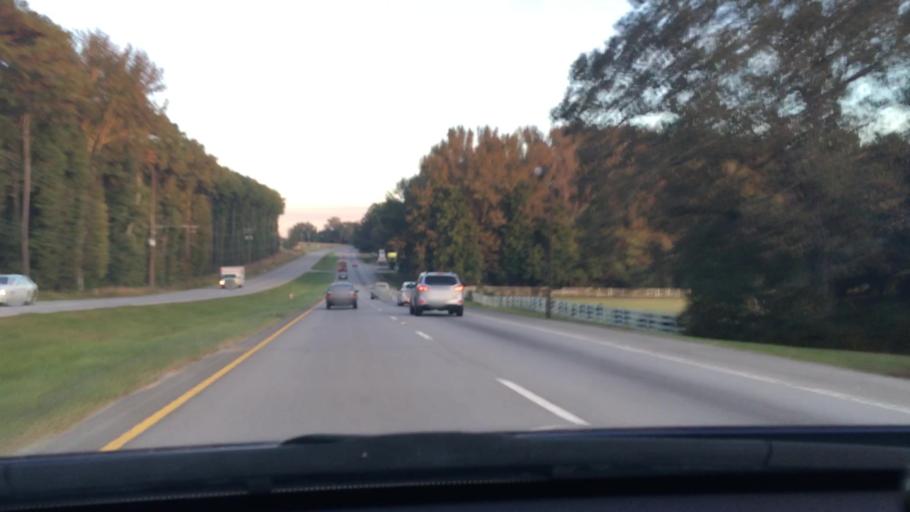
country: US
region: South Carolina
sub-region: Richland County
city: Hopkins
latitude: 33.9489
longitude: -80.8161
